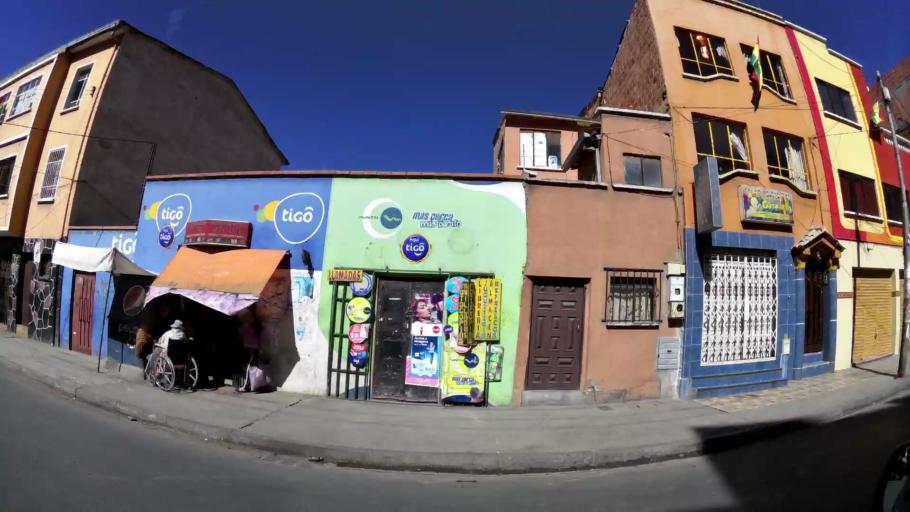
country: BO
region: La Paz
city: La Paz
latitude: -16.5077
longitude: -68.1430
